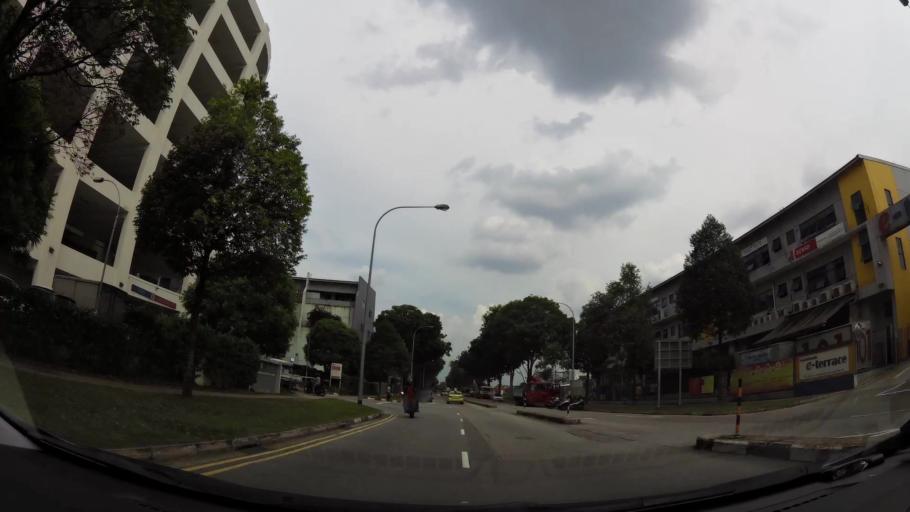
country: MY
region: Johor
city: Johor Bahru
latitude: 1.4503
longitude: 103.7916
